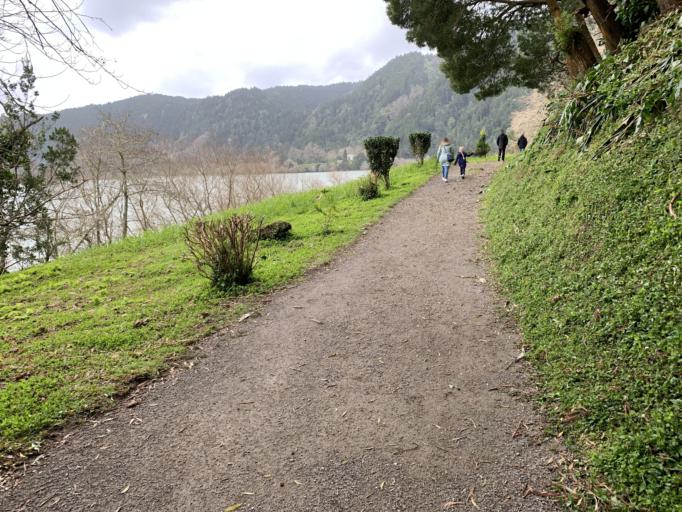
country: PT
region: Azores
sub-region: Povoacao
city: Furnas
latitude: 37.7639
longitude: -25.3367
